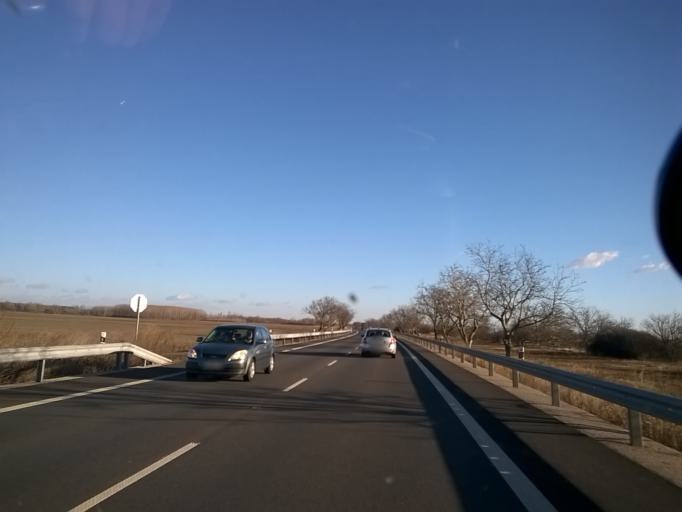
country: SK
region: Trnavsky
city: Sladkovicovo
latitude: 48.1982
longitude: 17.5694
